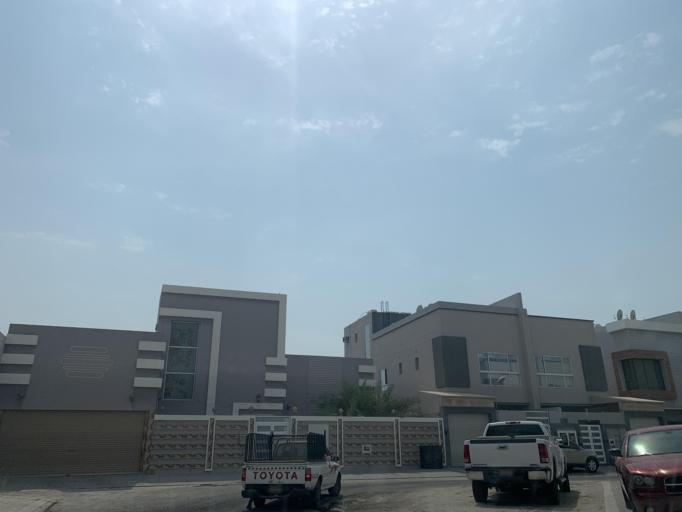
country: BH
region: Manama
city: Jidd Hafs
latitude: 26.2122
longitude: 50.4866
